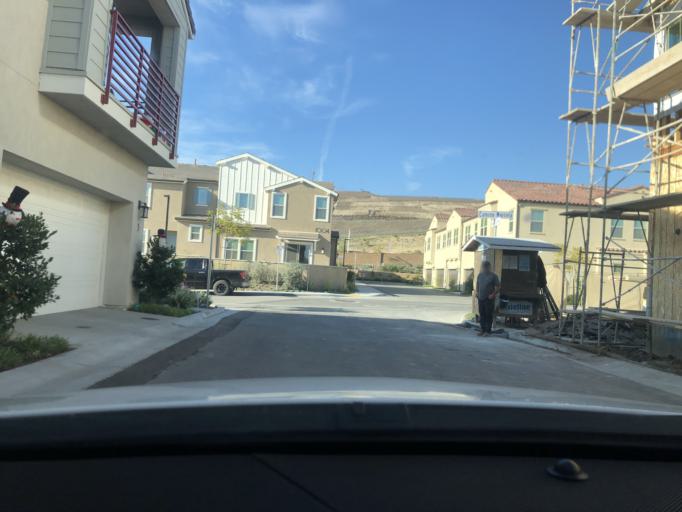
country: US
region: California
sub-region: San Diego County
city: Bonita
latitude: 32.5989
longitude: -117.0015
